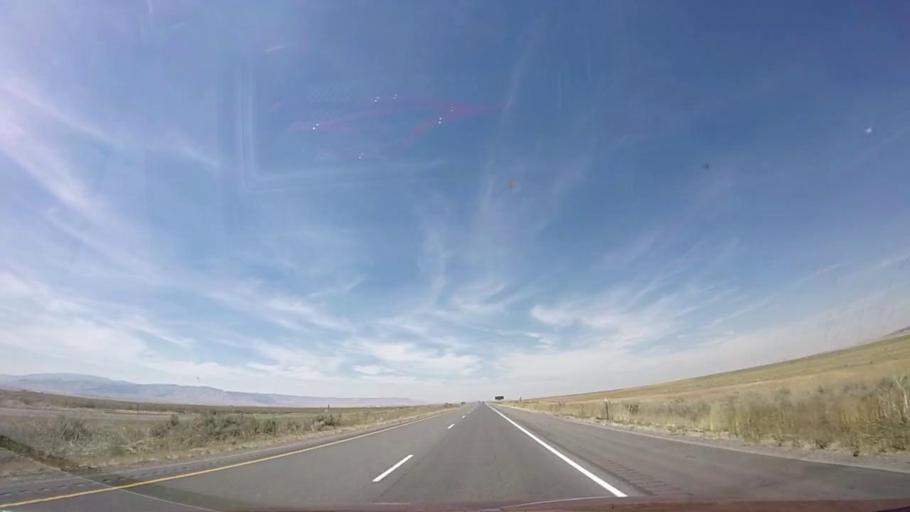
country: US
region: Idaho
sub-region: Power County
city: American Falls
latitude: 42.3038
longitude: -113.1825
